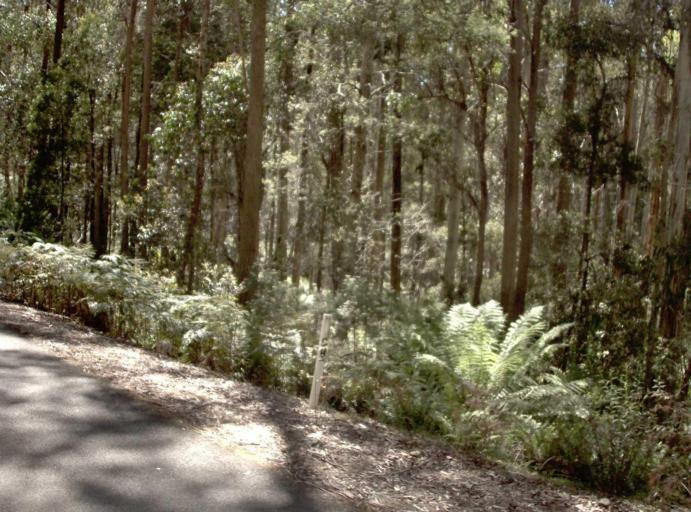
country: AU
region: New South Wales
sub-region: Bombala
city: Bombala
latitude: -37.0715
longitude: 148.7831
